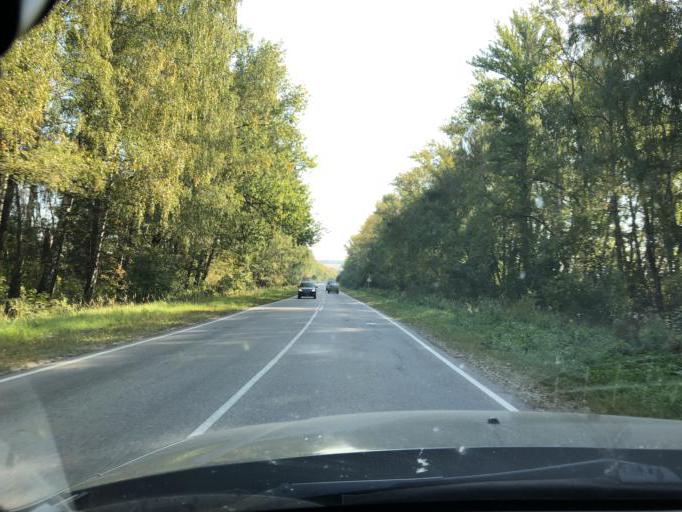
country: RU
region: Tula
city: Yasnogorsk
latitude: 54.4666
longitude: 37.6094
